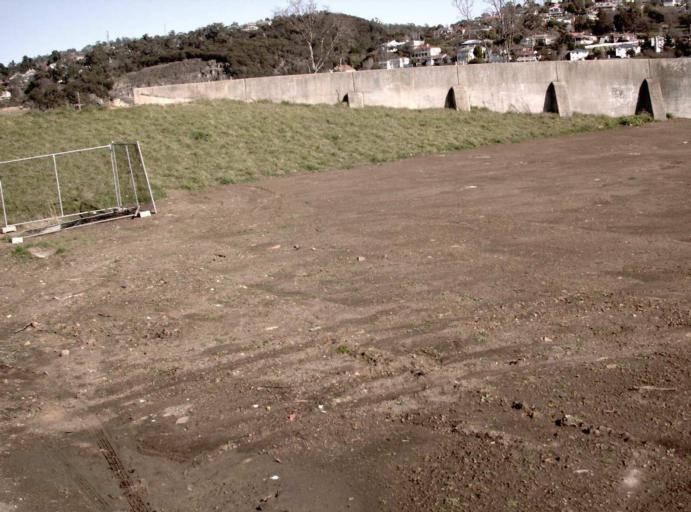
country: AU
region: Tasmania
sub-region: Launceston
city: Launceston
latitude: -41.4329
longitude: 147.1295
